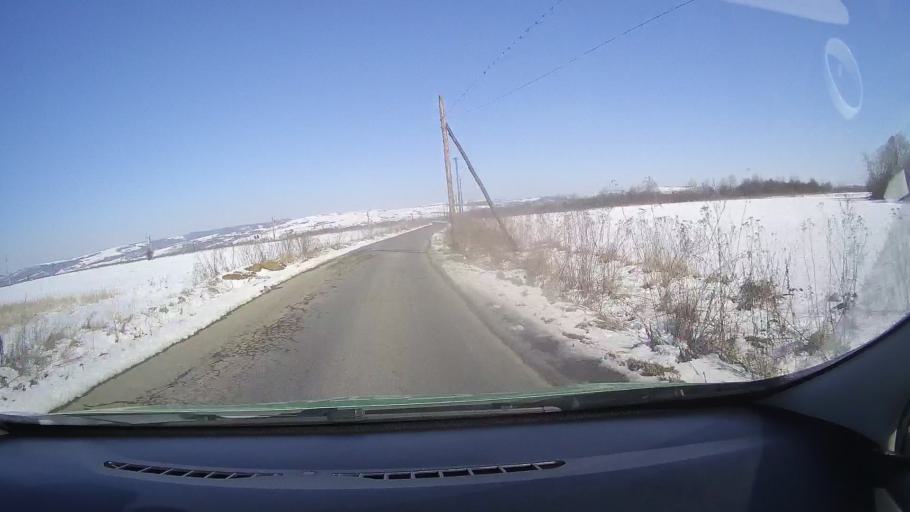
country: RO
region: Brasov
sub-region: Comuna Mandra
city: Mandra
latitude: 45.8280
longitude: 25.0113
